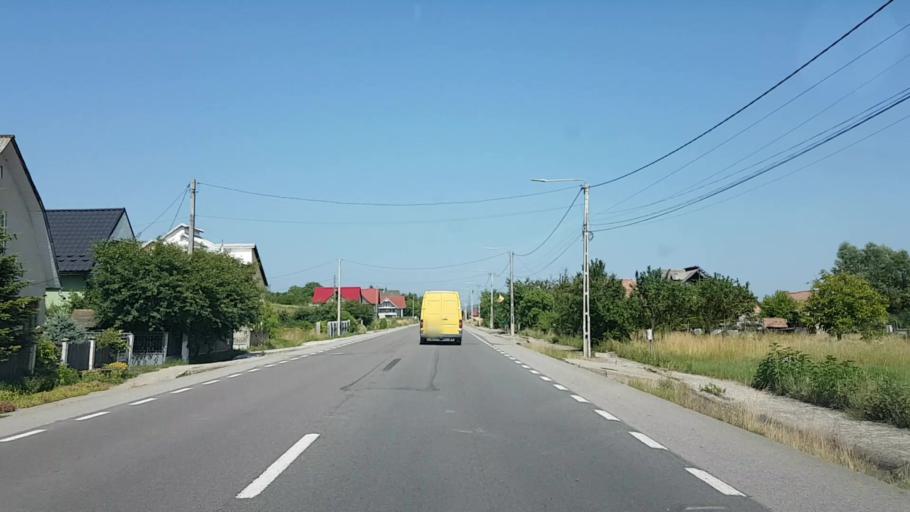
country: RO
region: Bistrita-Nasaud
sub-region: Comuna Ciceu-Mihaiesti
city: Ciceu-Mihaiesti
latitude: 47.1816
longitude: 23.9601
